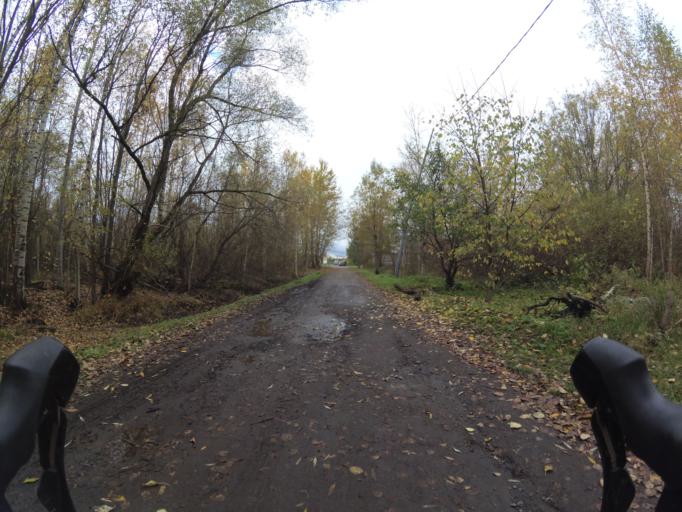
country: RU
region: St.-Petersburg
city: Lakhtinskiy
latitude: 59.9973
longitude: 30.1619
